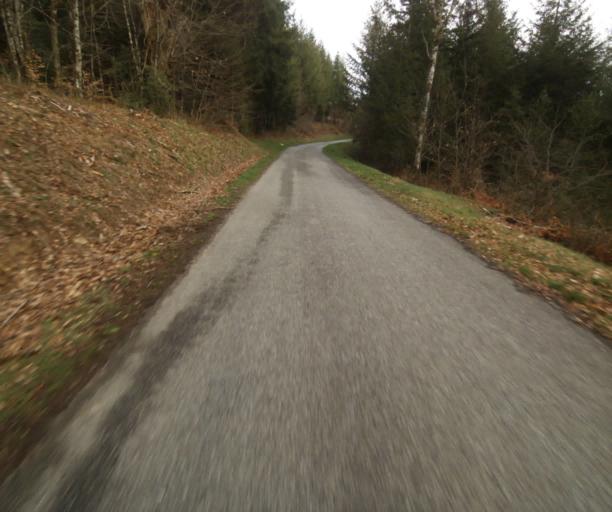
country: FR
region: Limousin
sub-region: Departement de la Correze
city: Saint-Privat
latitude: 45.2273
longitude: 1.9929
